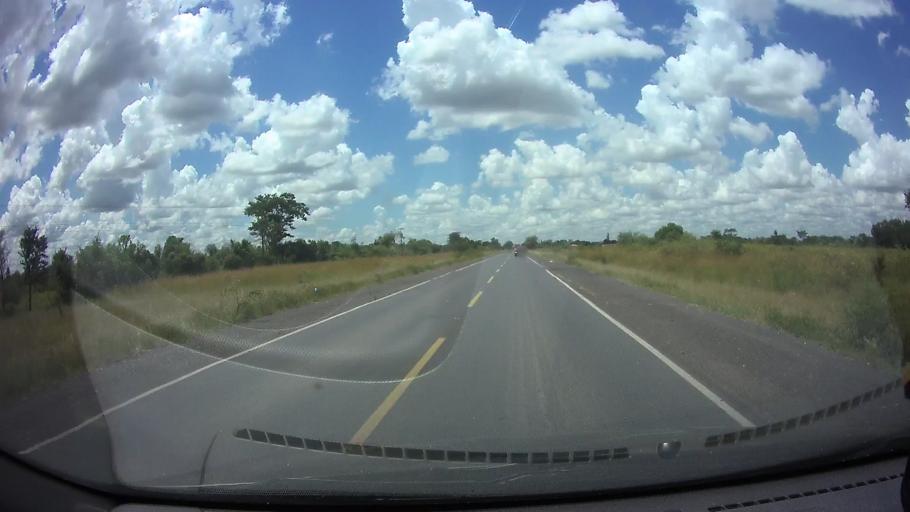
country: PY
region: Presidente Hayes
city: Nanawa
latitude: -25.2216
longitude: -57.6789
